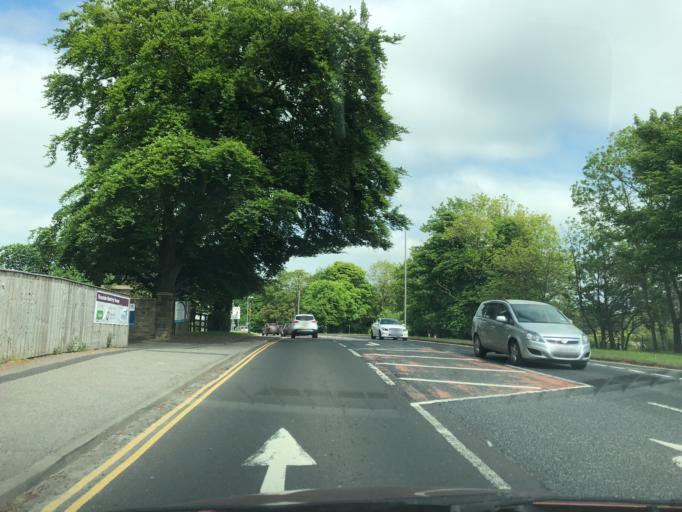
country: GB
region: England
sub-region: North Yorkshire
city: Catterick Garrison
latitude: 54.3745
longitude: -1.7118
